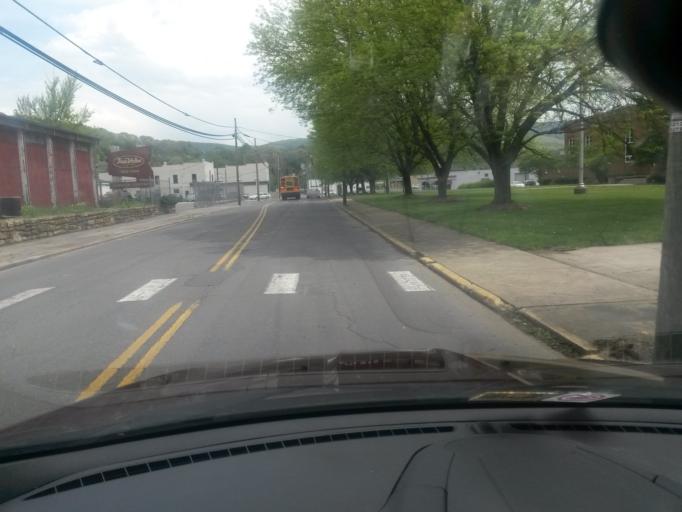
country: US
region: Virginia
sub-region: City of Covington
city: Covington
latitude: 37.7846
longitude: -79.9915
